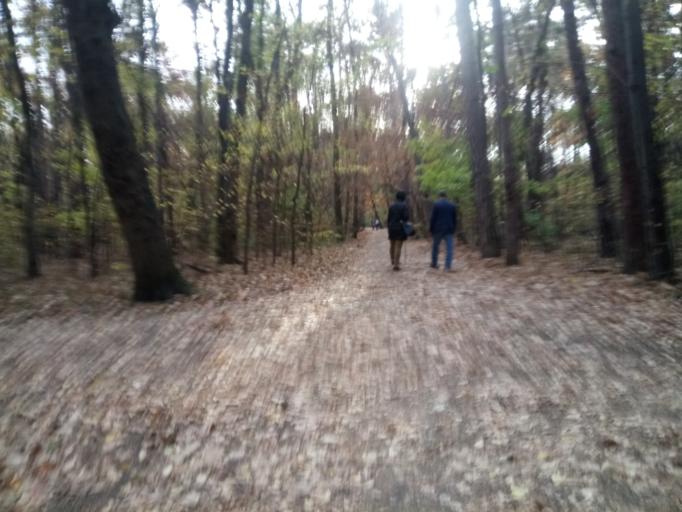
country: BG
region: Sofia-Capital
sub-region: Stolichna Obshtina
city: Sofia
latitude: 42.6802
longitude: 23.3461
